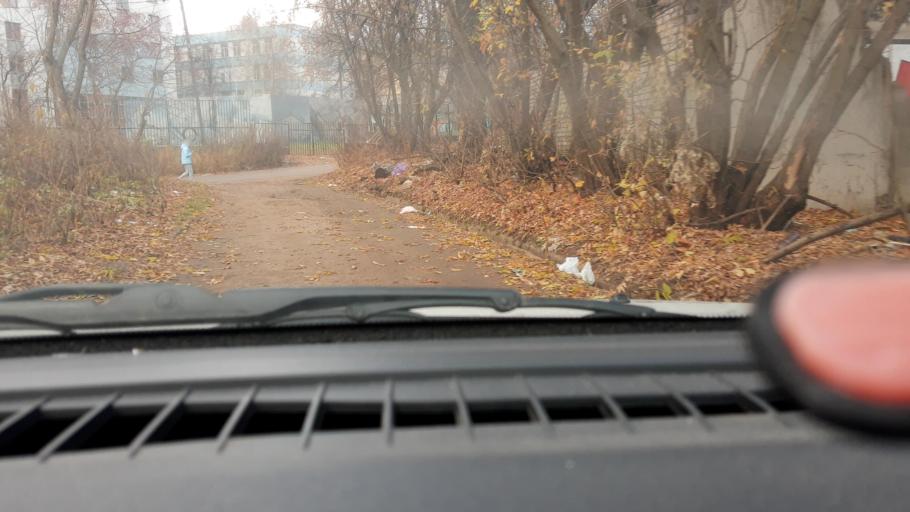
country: RU
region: Nizjnij Novgorod
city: Nizhniy Novgorod
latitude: 56.2973
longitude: 43.9769
